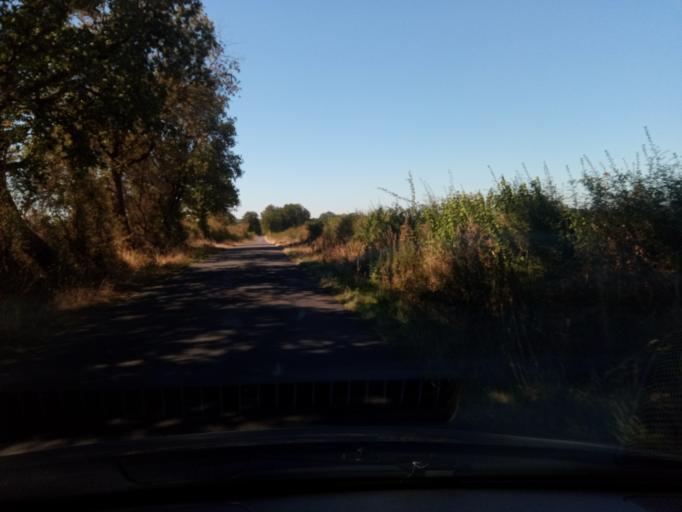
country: FR
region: Poitou-Charentes
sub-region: Departement de la Vienne
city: Montmorillon
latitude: 46.4807
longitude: 0.8606
